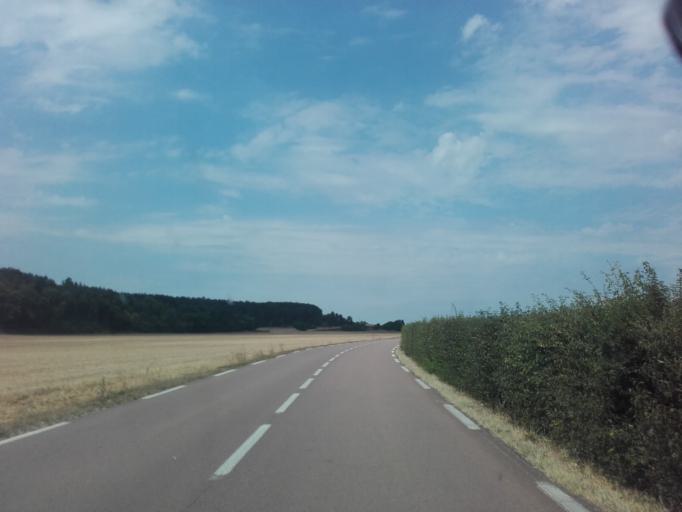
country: FR
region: Bourgogne
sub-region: Departement de l'Yonne
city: Chablis
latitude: 47.7795
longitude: 3.8076
